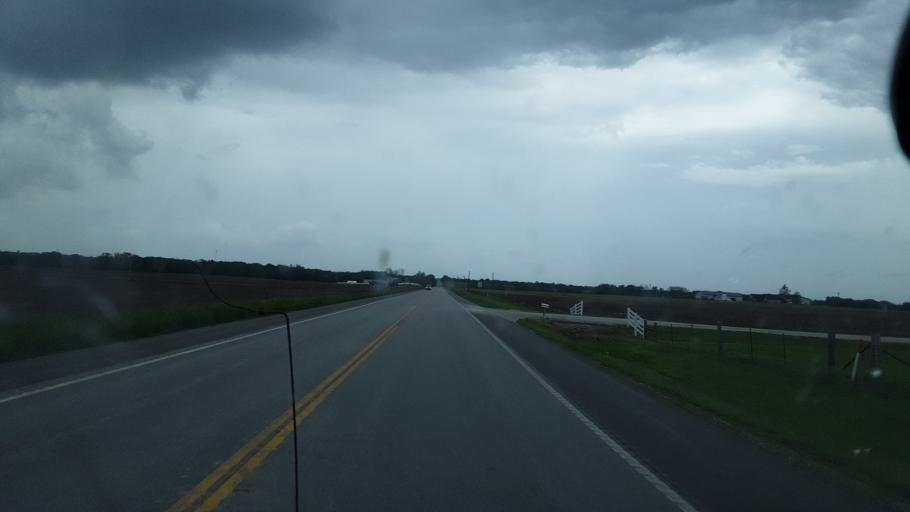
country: US
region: Missouri
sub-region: Marion County
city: Palmyra
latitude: 39.7346
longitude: -91.5099
